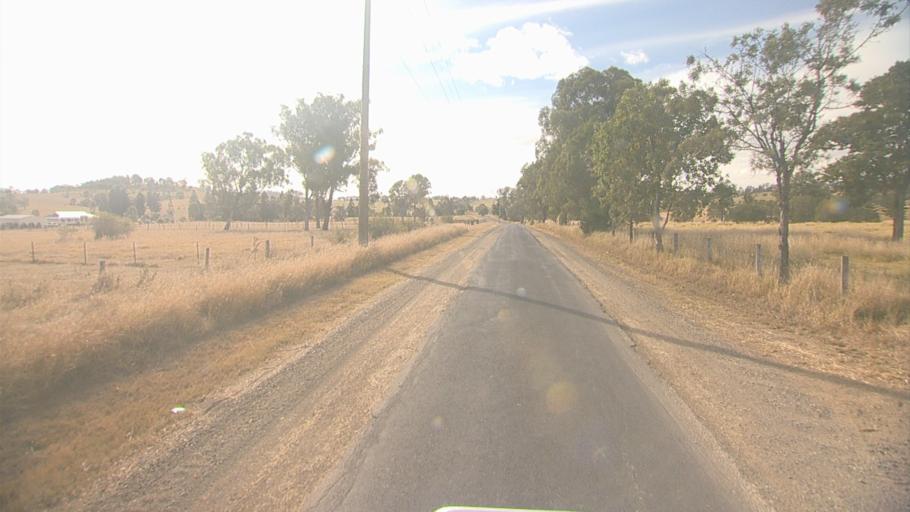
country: AU
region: Queensland
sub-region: Logan
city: Cedar Vale
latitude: -27.9170
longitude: 153.0134
